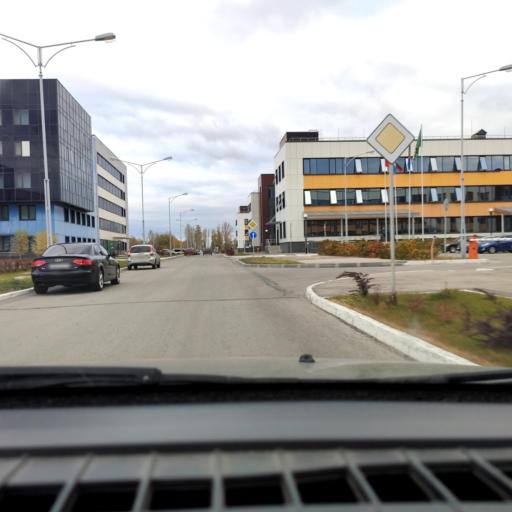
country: RU
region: Samara
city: Podstepki
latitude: 53.5554
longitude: 49.2153
